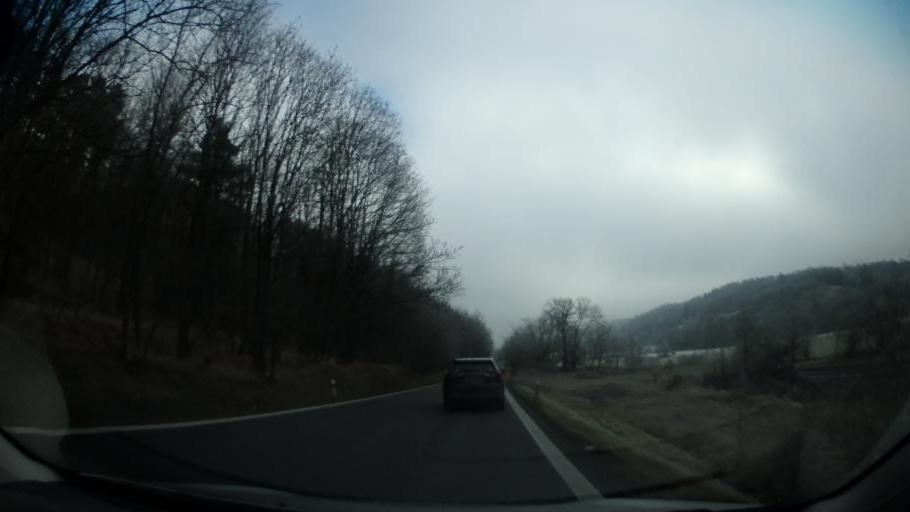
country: CZ
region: Vysocina
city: Vladislav
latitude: 49.2134
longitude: 15.9635
